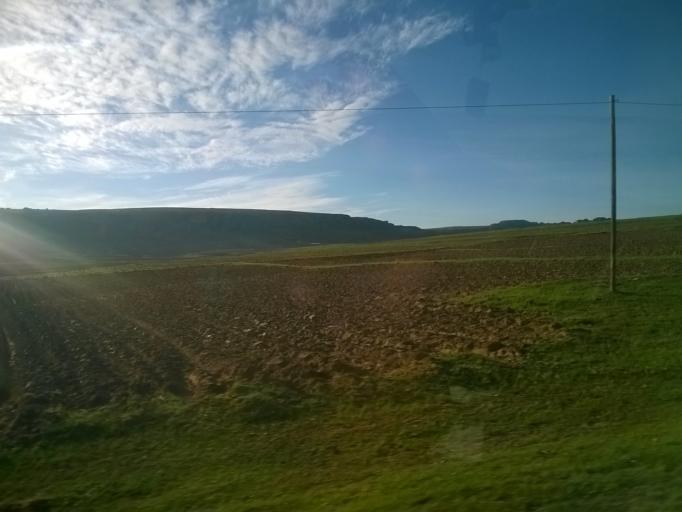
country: LS
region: Berea
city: Teyateyaneng
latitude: -29.1748
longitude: 27.6318
